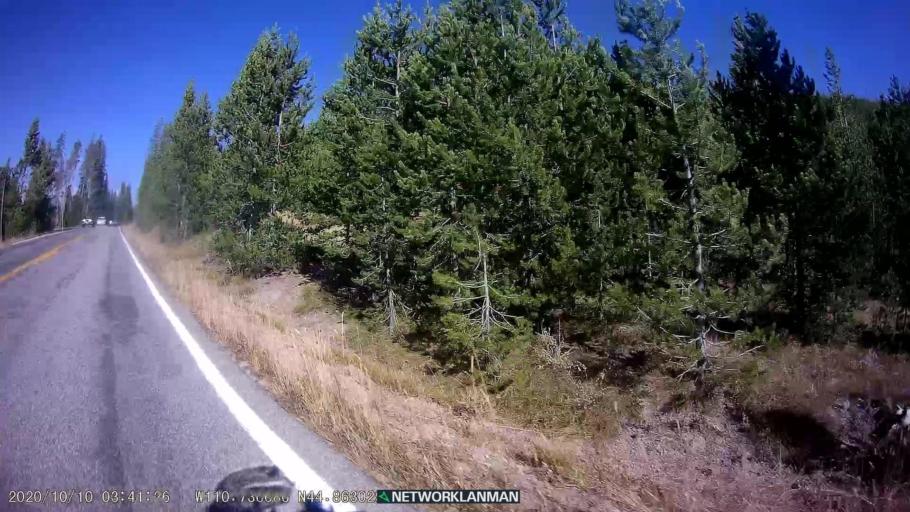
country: US
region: Montana
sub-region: Gallatin County
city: West Yellowstone
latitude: 44.8633
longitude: -110.7368
